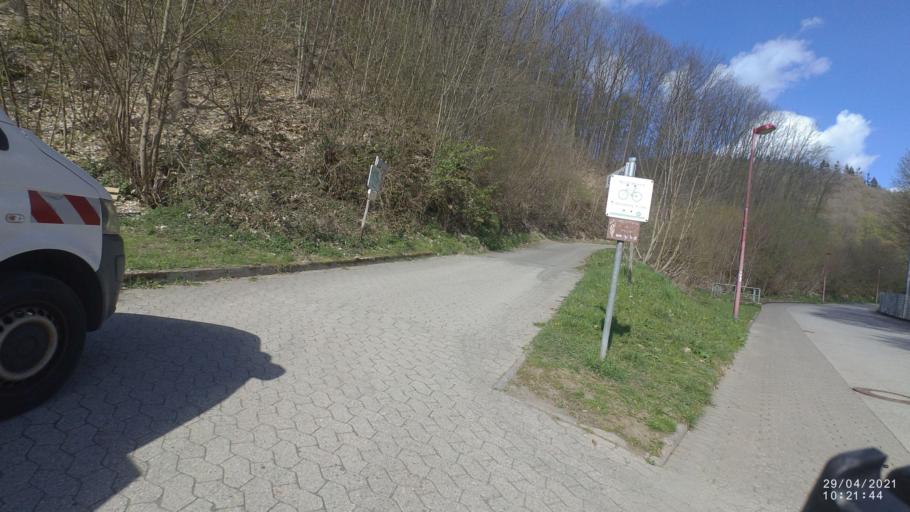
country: DE
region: Rheinland-Pfalz
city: Mayen
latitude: 50.3362
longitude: 7.2122
